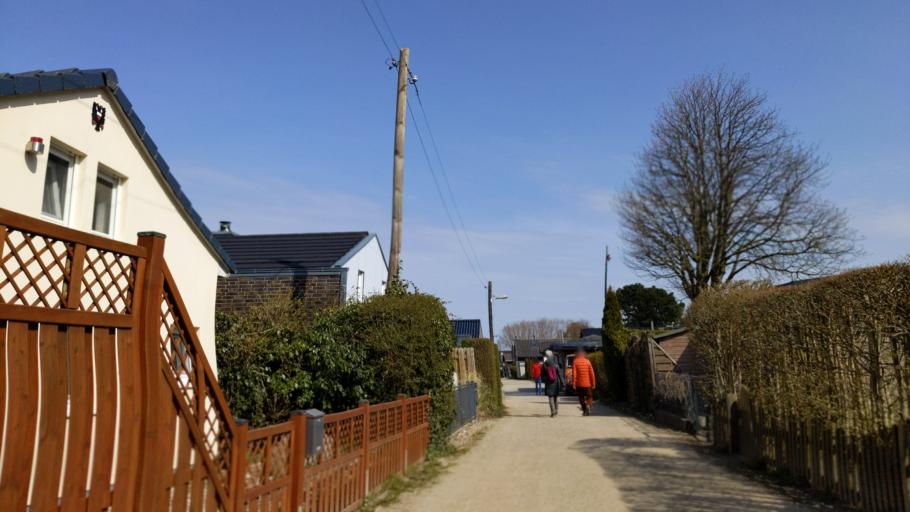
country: DE
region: Schleswig-Holstein
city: Travemuende
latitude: 53.9552
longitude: 10.8982
